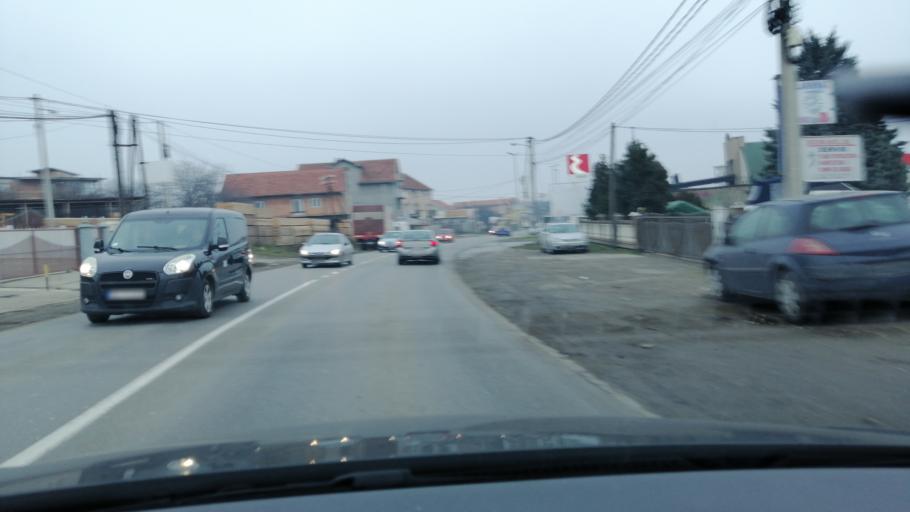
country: RS
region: Central Serbia
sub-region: Belgrade
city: Zvezdara
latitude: 44.7763
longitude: 20.5382
